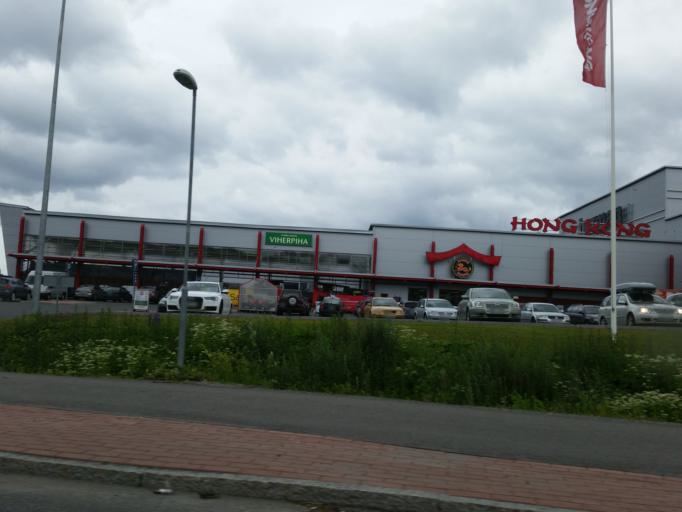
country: FI
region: Northern Savo
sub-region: Kuopio
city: Kuopio
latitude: 62.8735
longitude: 27.6230
